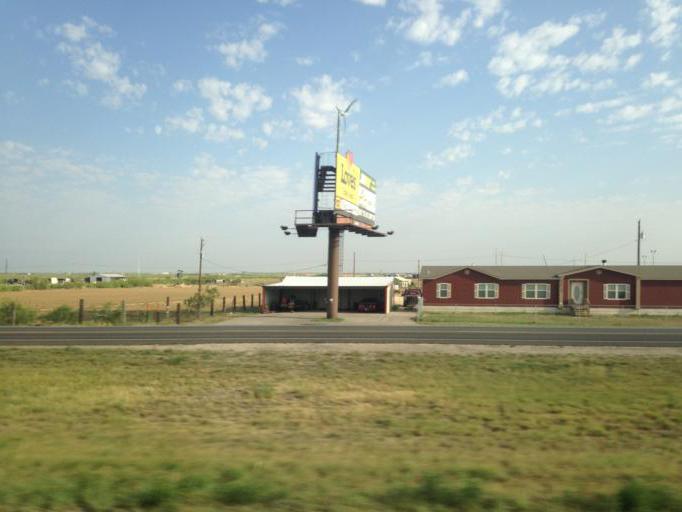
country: US
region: Texas
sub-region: Martin County
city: Stanton
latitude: 32.0706
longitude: -101.9295
